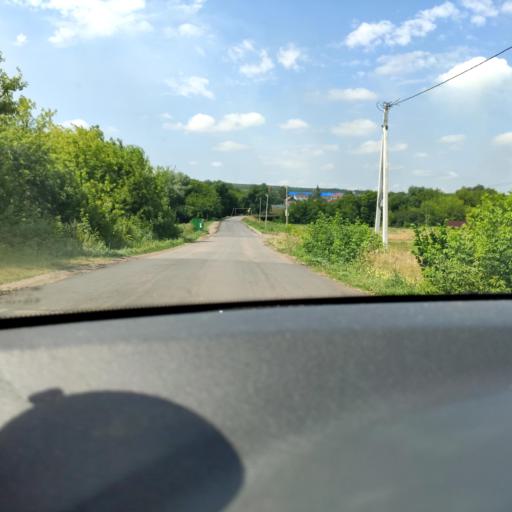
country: RU
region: Samara
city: Kinel'
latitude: 53.3390
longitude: 50.5294
